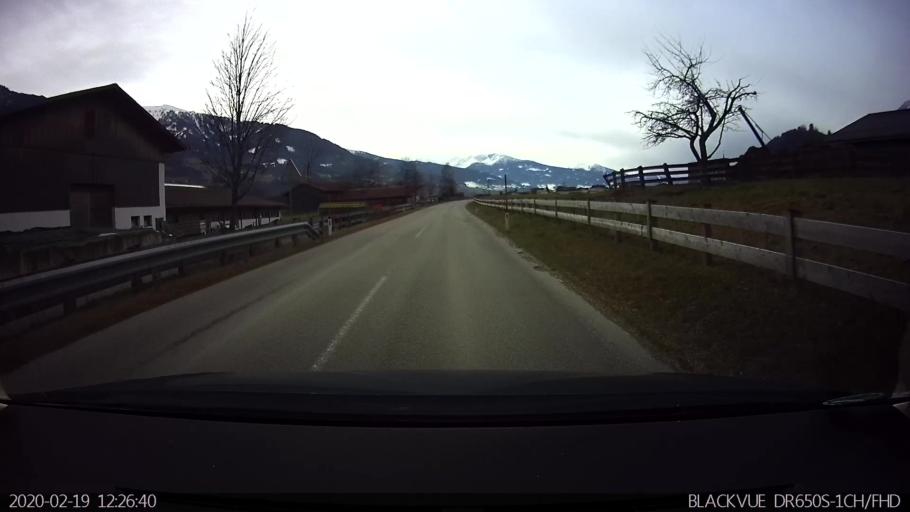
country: AT
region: Tyrol
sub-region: Politischer Bezirk Schwaz
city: Stans
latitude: 47.3735
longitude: 11.7246
